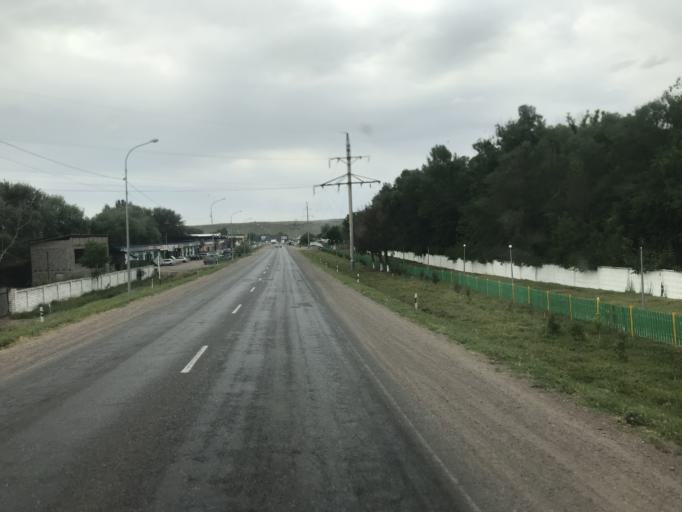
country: KZ
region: Ongtustik Qazaqstan
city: Saryaghash
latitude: 41.4903
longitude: 69.2673
